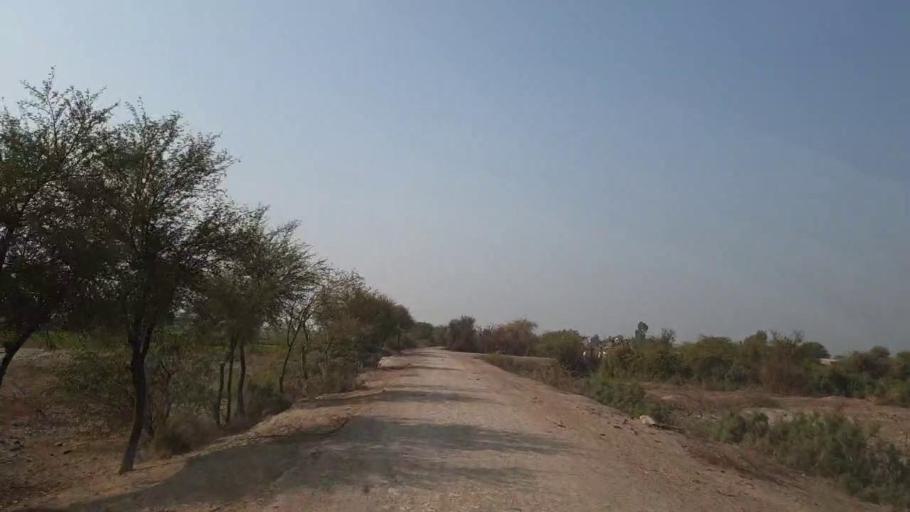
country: PK
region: Sindh
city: Pithoro
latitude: 25.6948
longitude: 69.2104
